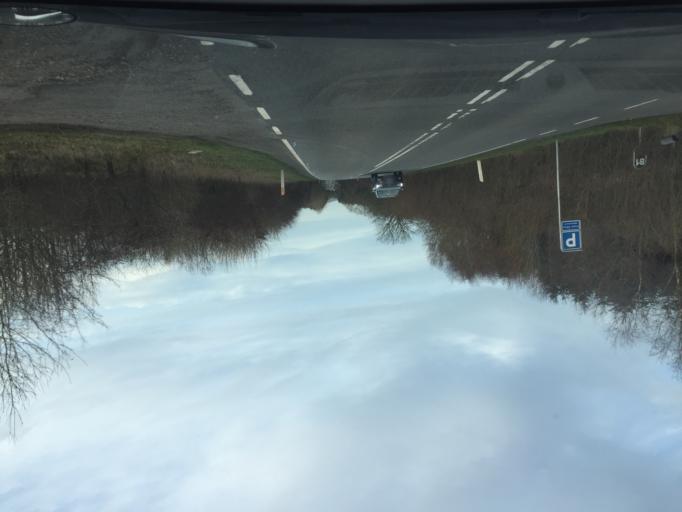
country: DK
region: South Denmark
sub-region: Faaborg-Midtfyn Kommune
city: Ringe
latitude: 55.2089
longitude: 10.4073
